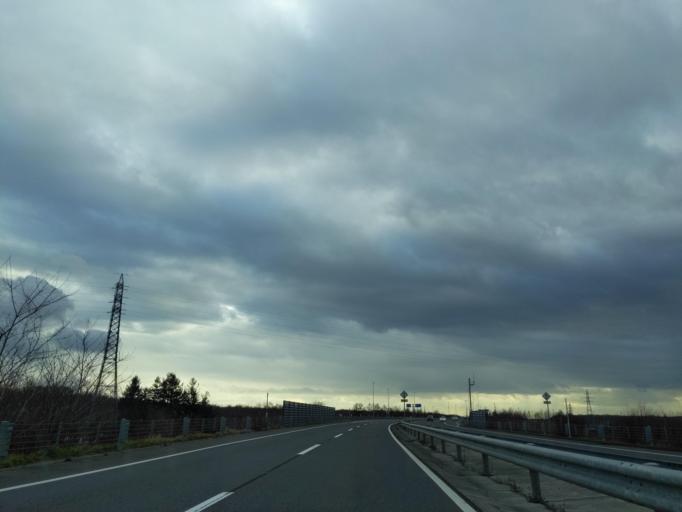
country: JP
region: Hokkaido
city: Chitose
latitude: 42.8295
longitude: 141.6899
